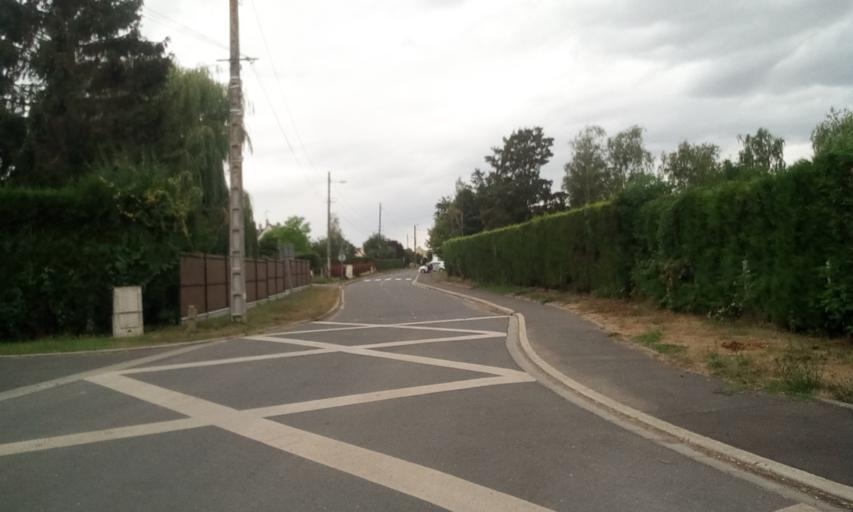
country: FR
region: Lower Normandy
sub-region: Departement du Calvados
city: Bellengreville
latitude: 49.1494
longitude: -0.2242
